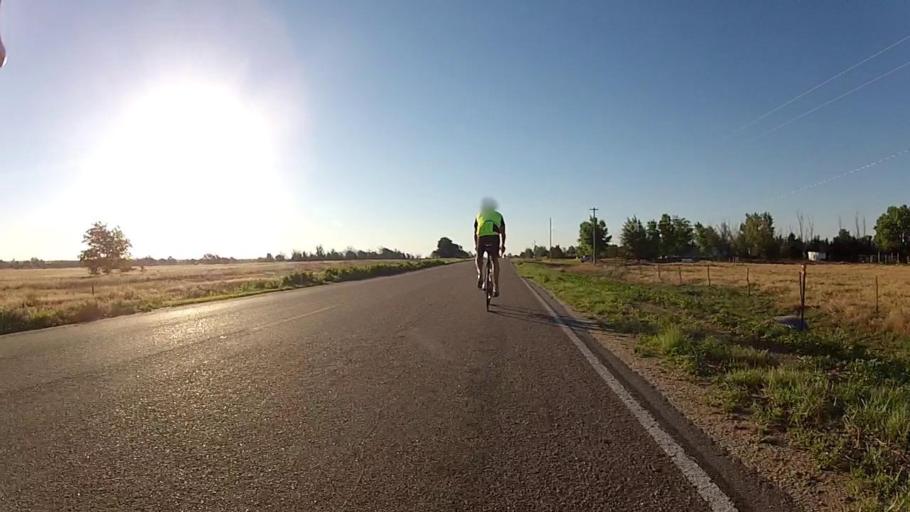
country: US
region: Kansas
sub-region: Ford County
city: Dodge City
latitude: 37.7092
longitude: -99.9135
